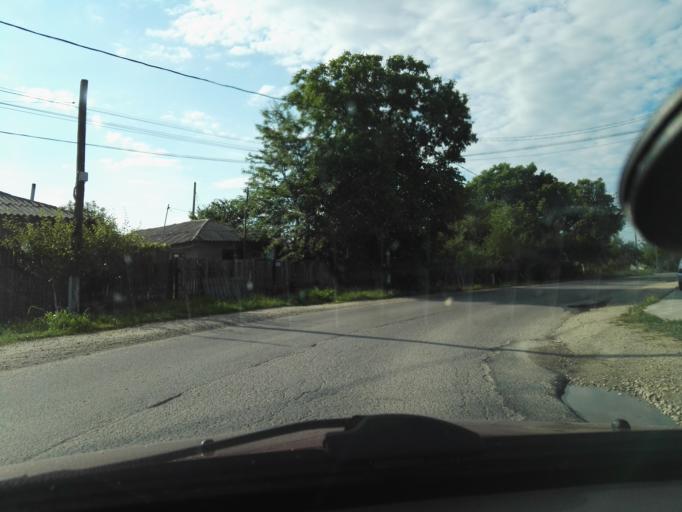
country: RO
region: Ilfov
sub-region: Comuna Copaceni
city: Copaceni
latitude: 44.2445
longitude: 26.0893
